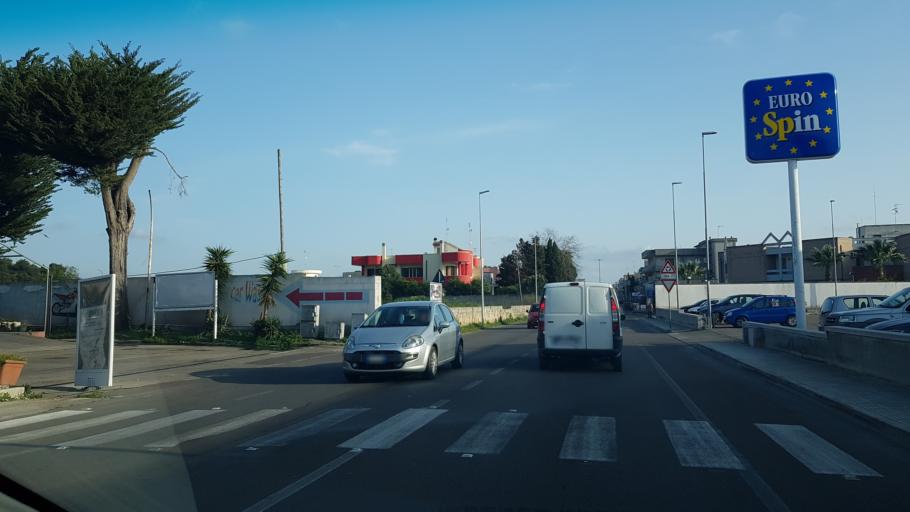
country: IT
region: Apulia
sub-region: Provincia di Lecce
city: Trepuzzi
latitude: 40.4110
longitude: 18.0662
